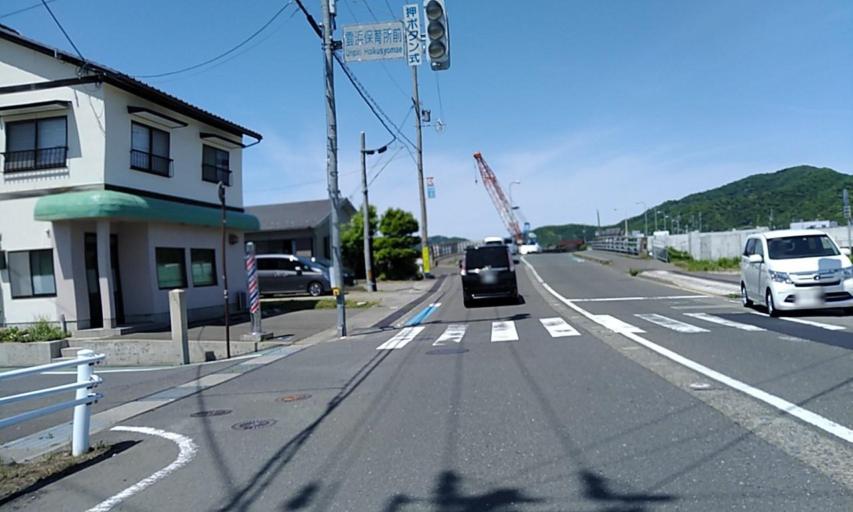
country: JP
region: Fukui
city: Obama
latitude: 35.5036
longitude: 135.7472
